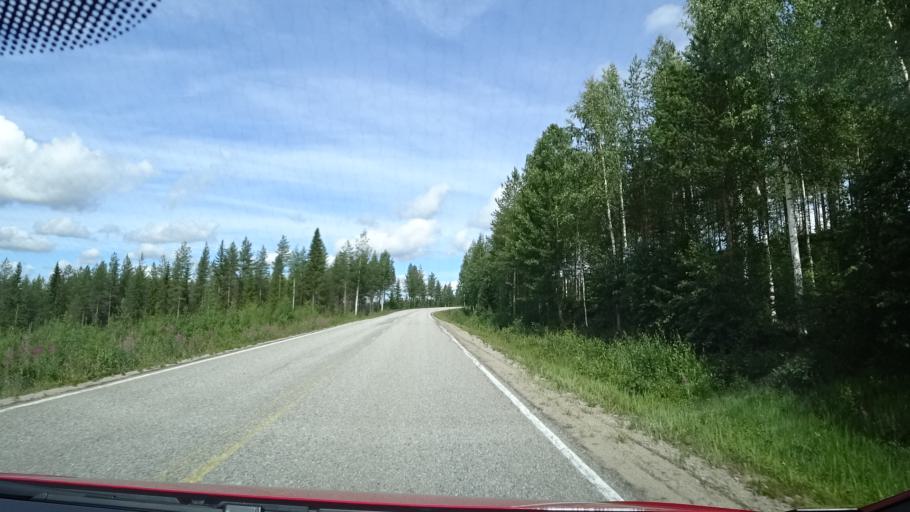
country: FI
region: Kainuu
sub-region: Kehys-Kainuu
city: Kuhmo
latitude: 64.4332
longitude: 29.8100
